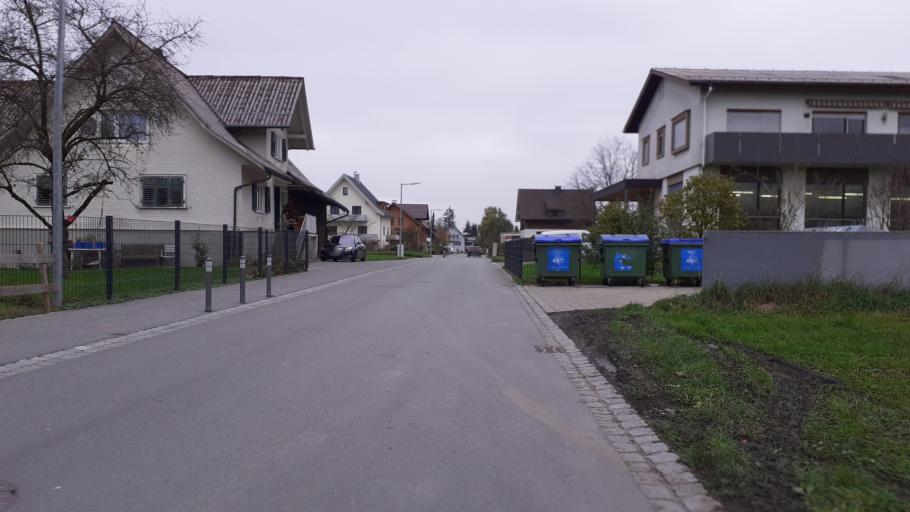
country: AT
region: Vorarlberg
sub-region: Politischer Bezirk Dornbirn
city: Lustenau
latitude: 47.4221
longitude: 9.6670
